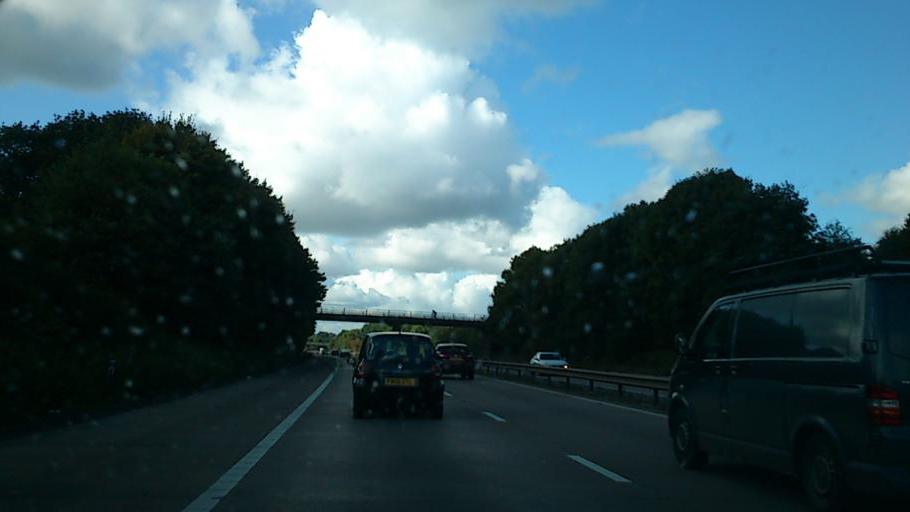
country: GB
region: England
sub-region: Staffordshire
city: Codsall
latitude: 52.6440
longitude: -2.1799
